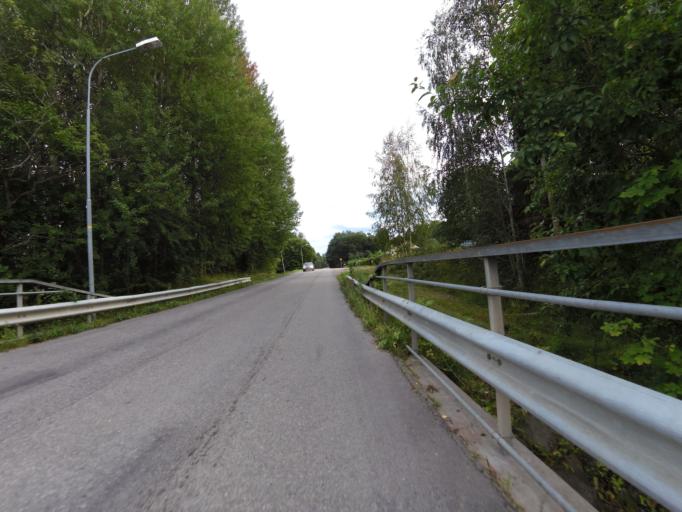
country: SE
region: Gaevleborg
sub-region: Gavle Kommun
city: Valbo
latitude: 60.6524
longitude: 17.0140
